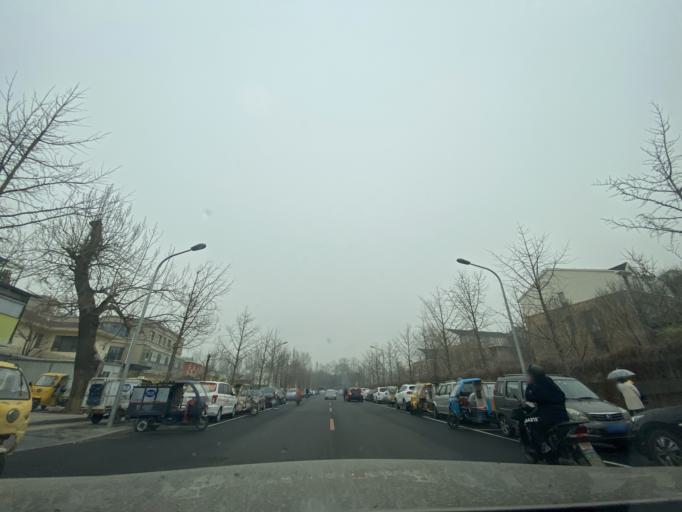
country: CN
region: Beijing
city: Sijiqing
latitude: 39.9568
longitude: 116.2283
